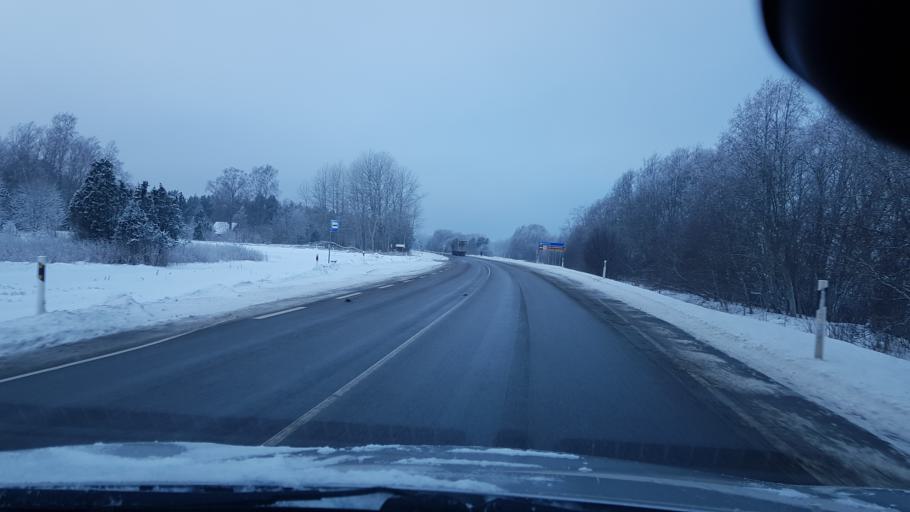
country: EE
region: Harju
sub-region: Paldiski linn
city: Paldiski
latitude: 59.3421
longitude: 24.1971
